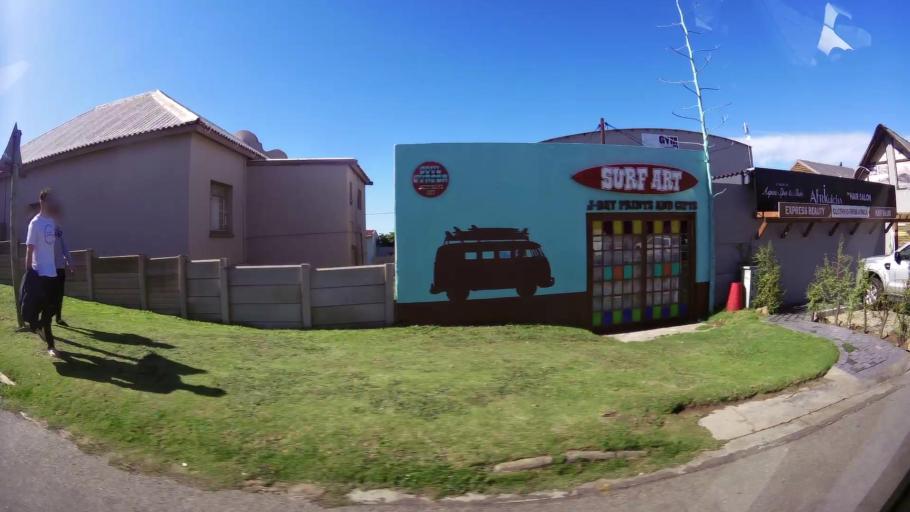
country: ZA
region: Eastern Cape
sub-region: Cacadu District Municipality
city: Jeffrey's Bay
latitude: -34.0563
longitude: 24.9226
